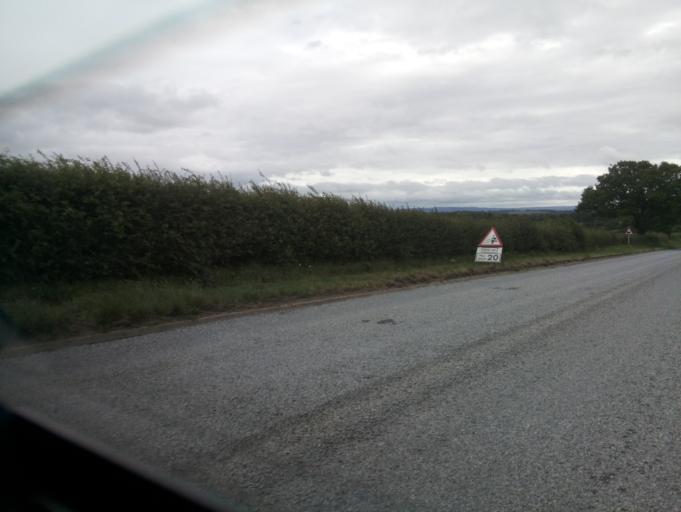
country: GB
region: England
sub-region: Worcestershire
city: Upton upon Severn
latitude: 52.0849
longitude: -2.2025
